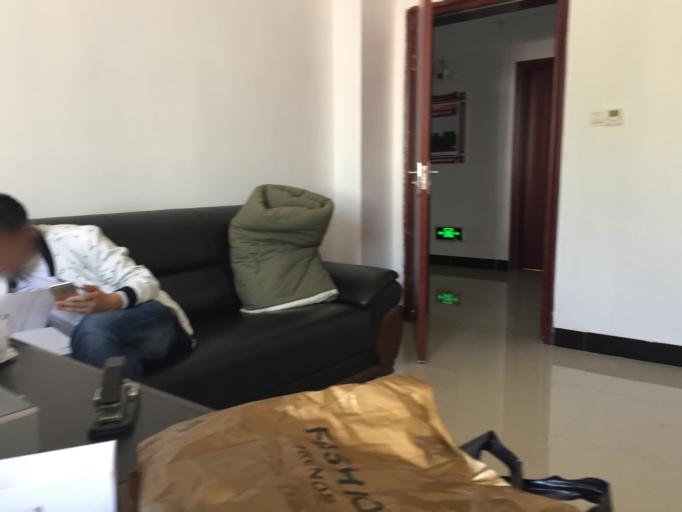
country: CN
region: Guizhou Sheng
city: Zhongba
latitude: 27.9659
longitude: 108.2554
